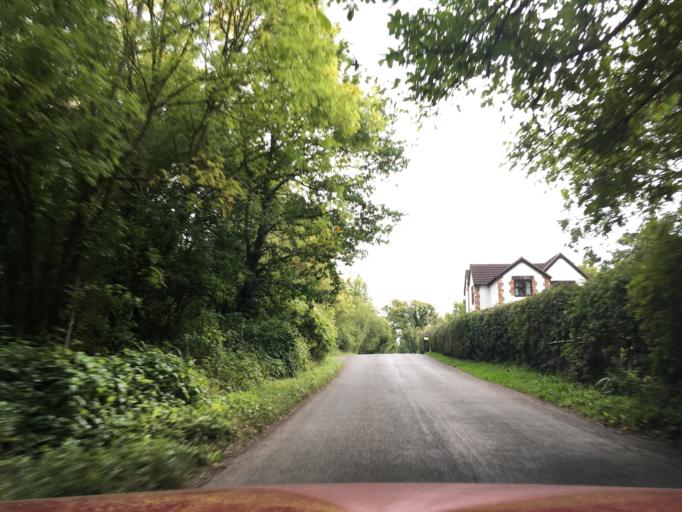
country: GB
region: England
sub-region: South Gloucestershire
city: Charfield
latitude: 51.6672
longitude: -2.4203
